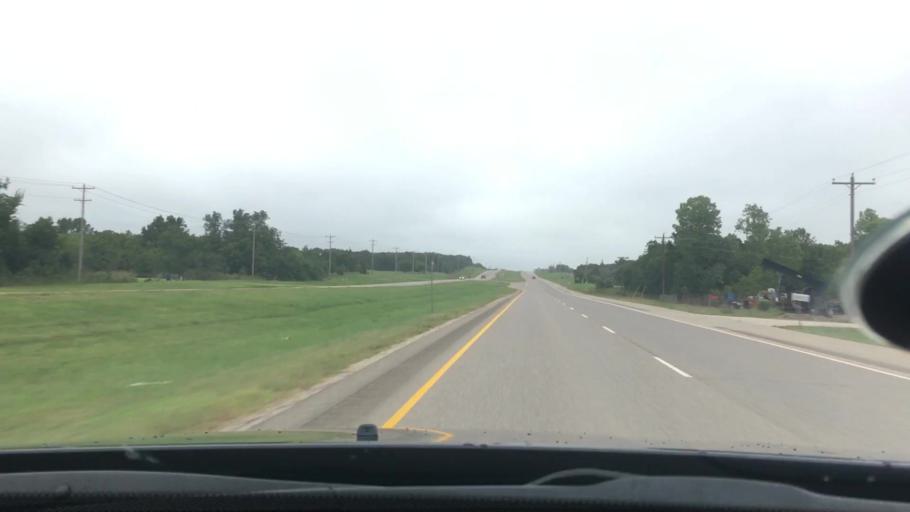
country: US
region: Oklahoma
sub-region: Seminole County
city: Seminole
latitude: 35.3233
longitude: -96.6713
